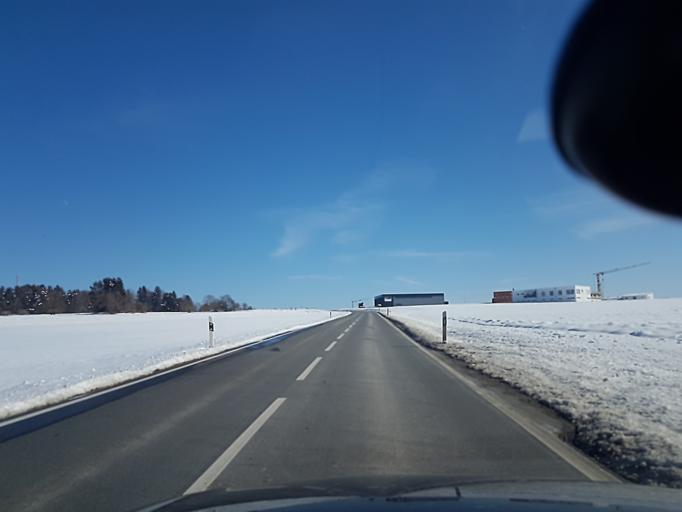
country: DE
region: Baden-Wuerttemberg
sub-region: Freiburg Region
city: Zimmern ob Rottweil
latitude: 48.1701
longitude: 8.5548
